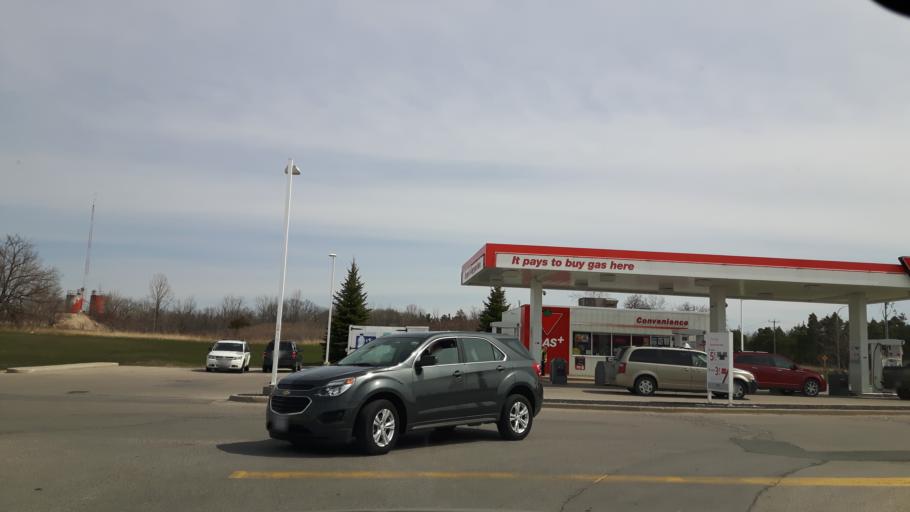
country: CA
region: Ontario
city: Goderich
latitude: 43.7301
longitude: -81.6879
